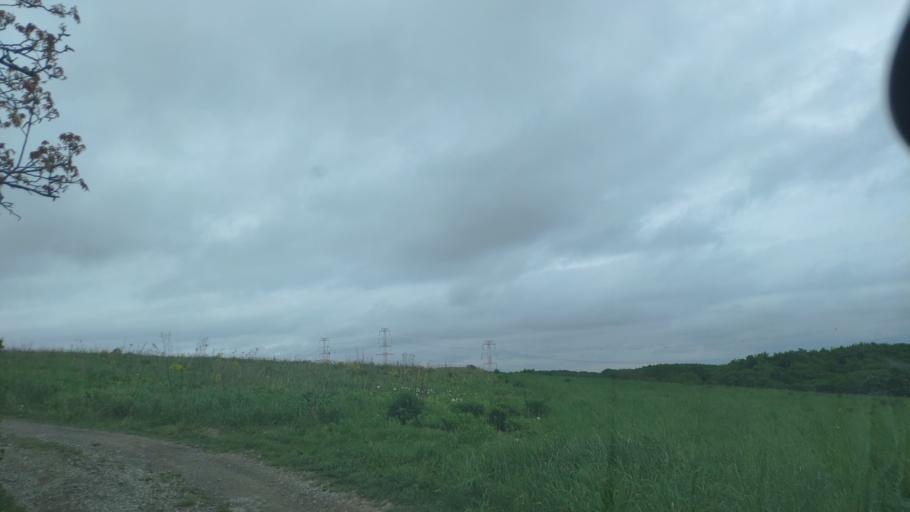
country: SK
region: Kosicky
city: Kosice
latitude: 48.7586
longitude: 21.1998
